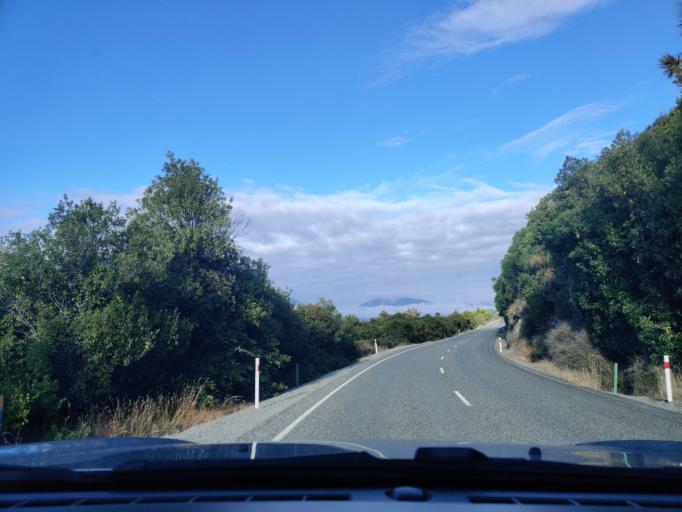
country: NZ
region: Otago
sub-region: Queenstown-Lakes District
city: Queenstown
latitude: -45.0556
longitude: 168.6137
